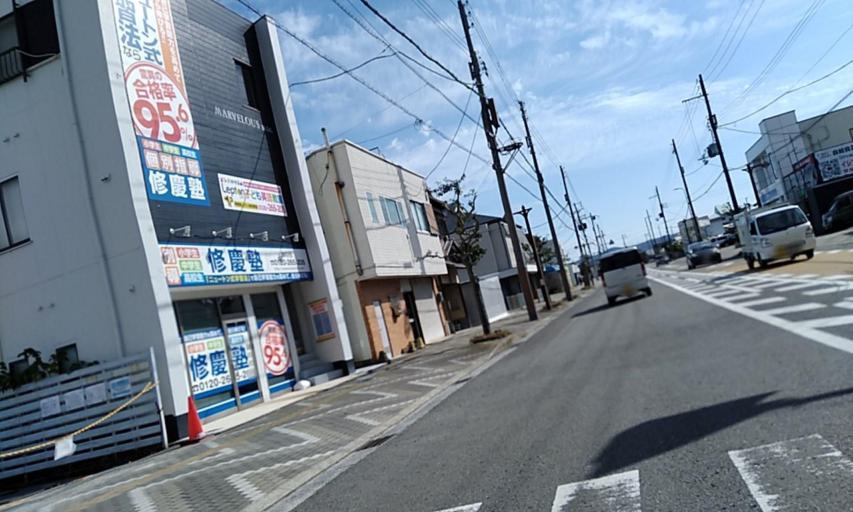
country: JP
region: Wakayama
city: Gobo
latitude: 33.9069
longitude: 135.1598
